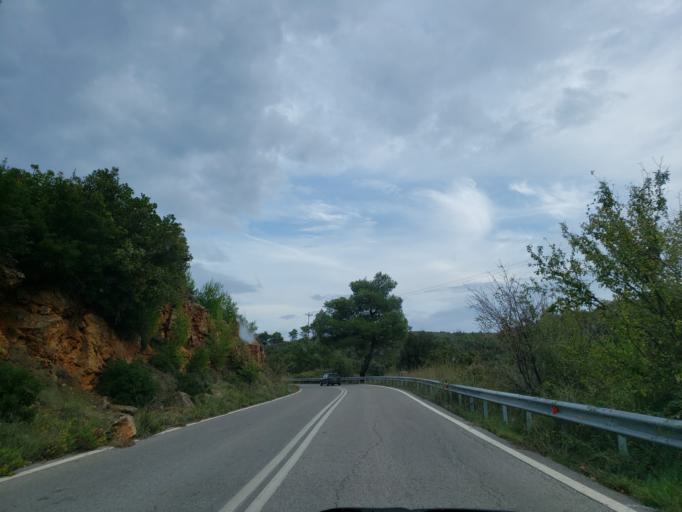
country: GR
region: Attica
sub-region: Nomarchia Anatolikis Attikis
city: Varnavas
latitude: 38.2194
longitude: 23.9323
